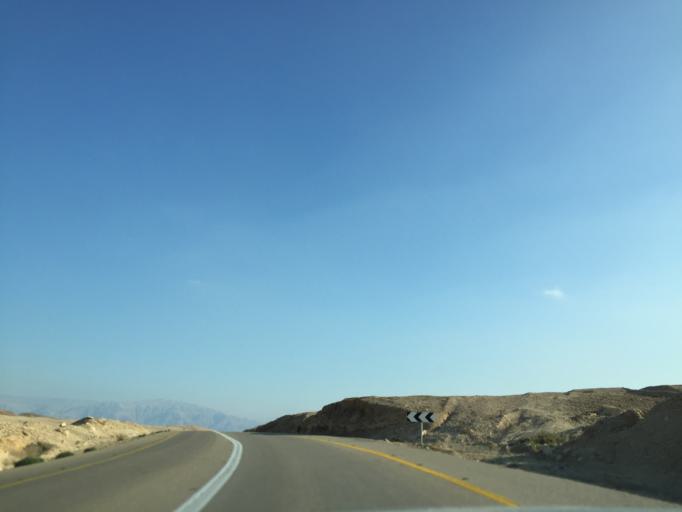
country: IL
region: Southern District
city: `En Boqeq
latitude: 31.1727
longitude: 35.3116
